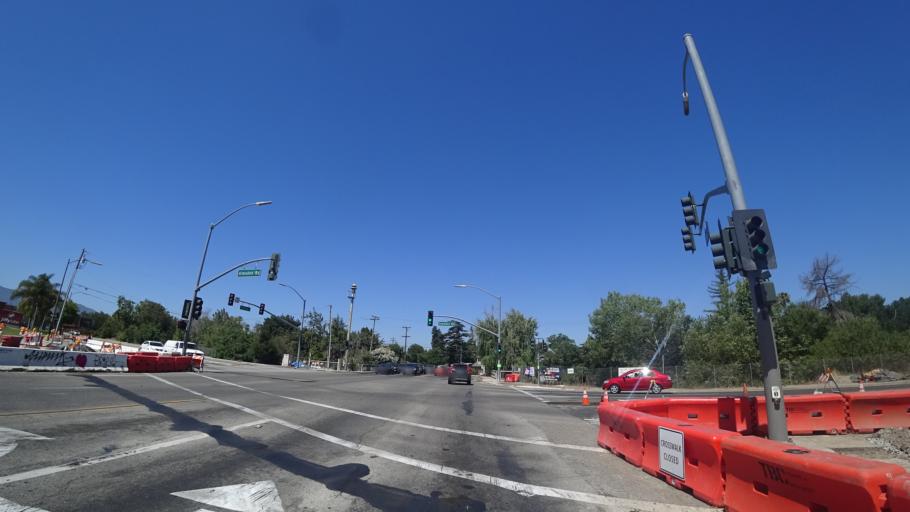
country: US
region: California
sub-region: Santa Clara County
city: Seven Trees
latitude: 37.2924
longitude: -121.8799
